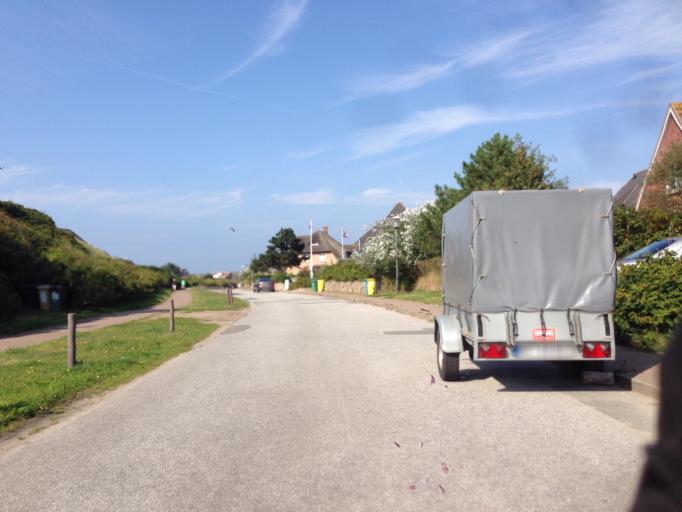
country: DE
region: Schleswig-Holstein
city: Westerland
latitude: 54.8489
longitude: 8.2944
